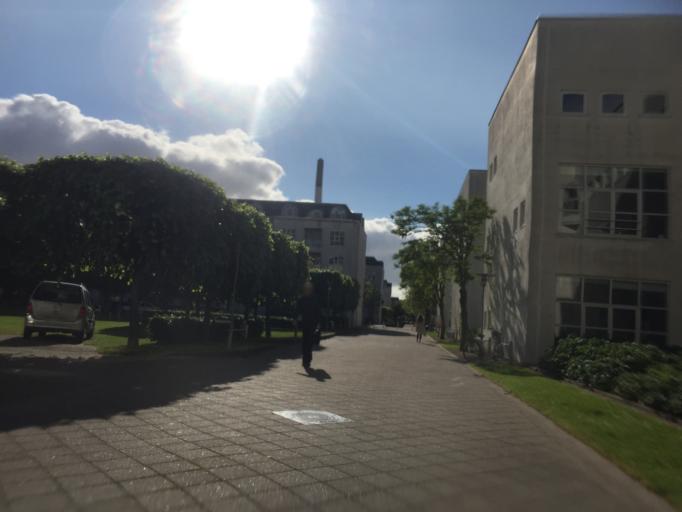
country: DK
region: Capital Region
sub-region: Frederiksberg Kommune
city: Frederiksberg
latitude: 55.6841
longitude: 12.5137
